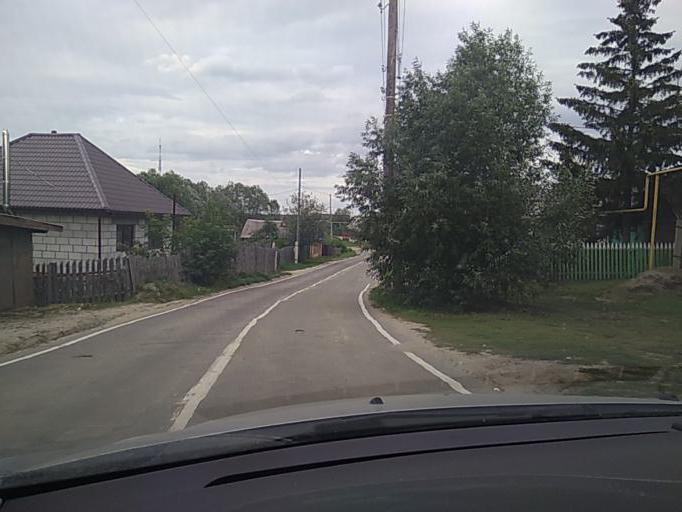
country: RU
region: Chelyabinsk
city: Kyshtym
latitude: 55.6939
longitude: 60.5324
